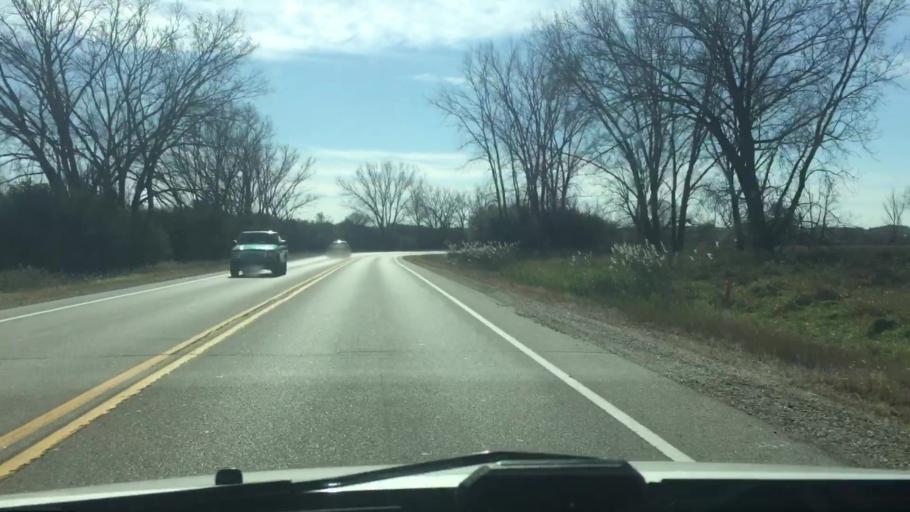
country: US
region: Wisconsin
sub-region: Waukesha County
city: Pewaukee
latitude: 43.0546
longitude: -88.2521
